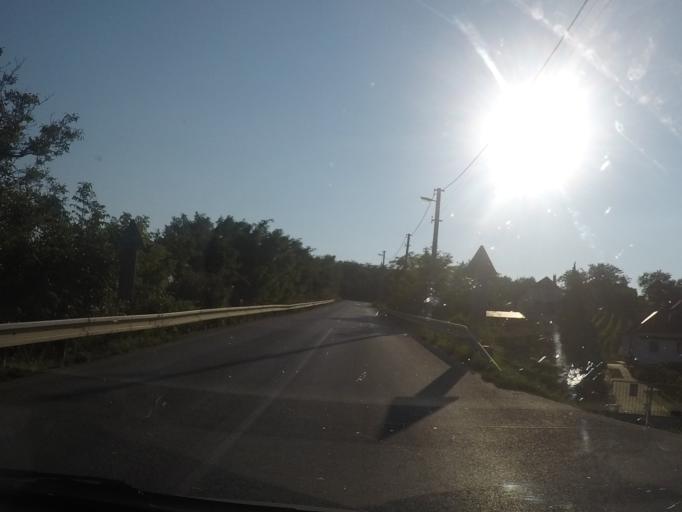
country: SK
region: Nitriansky
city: Zlate Moravce
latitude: 48.3879
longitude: 18.3745
